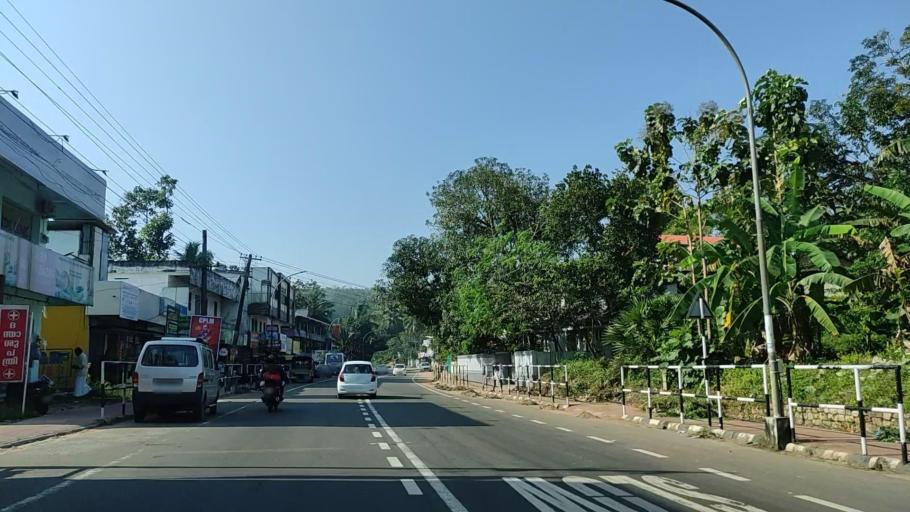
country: IN
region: Kerala
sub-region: Kollam
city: Punalur
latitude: 8.9248
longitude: 76.8545
